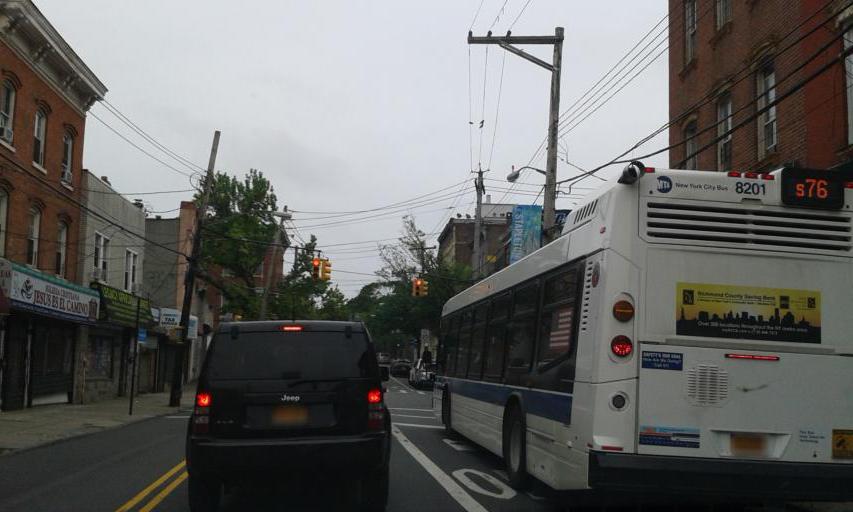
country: US
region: New Jersey
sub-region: Hudson County
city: Bayonne
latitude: 40.6260
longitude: -74.0753
